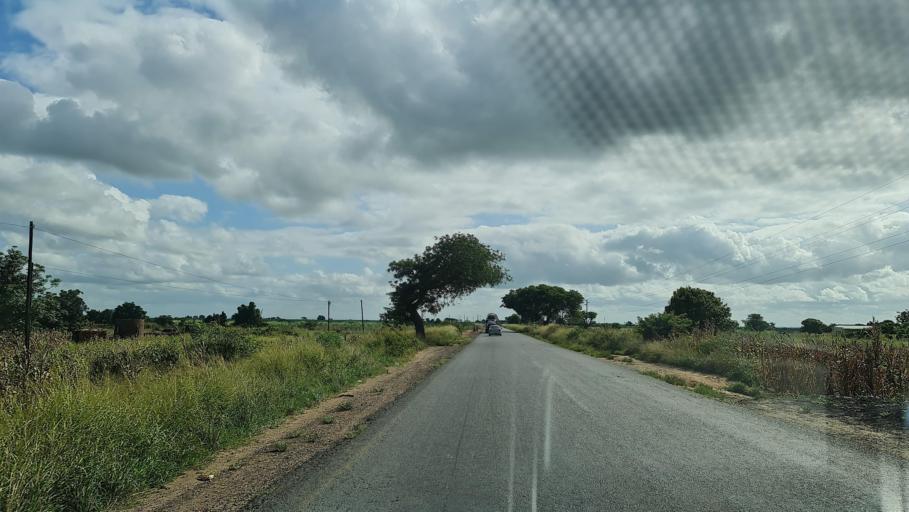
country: MZ
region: Gaza
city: Macia
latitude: -25.0824
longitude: 32.8478
